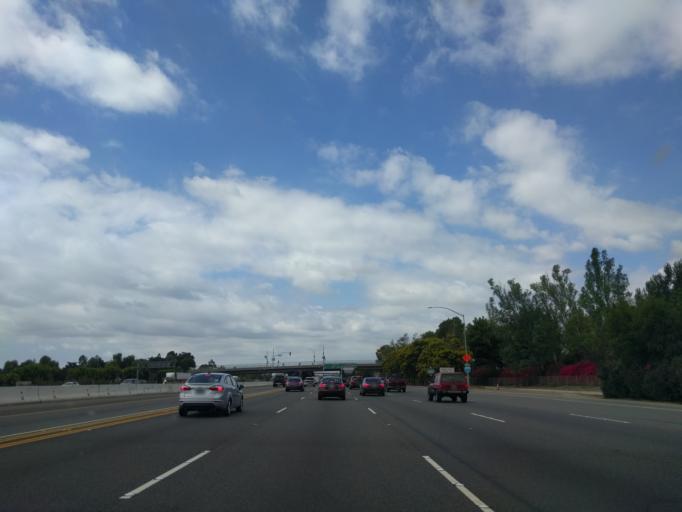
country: US
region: California
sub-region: Orange County
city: Laguna Woods
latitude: 33.6584
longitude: -117.7458
